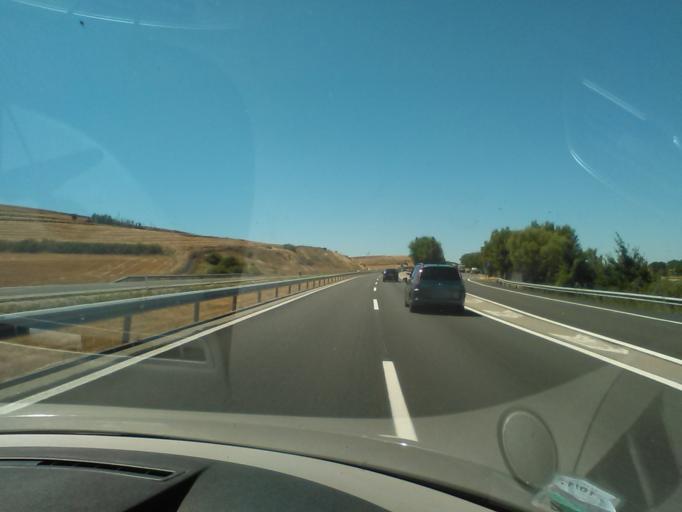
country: ES
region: Castille and Leon
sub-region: Provincia de Burgos
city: Villanueva de Teba
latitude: 42.6231
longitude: -3.1642
